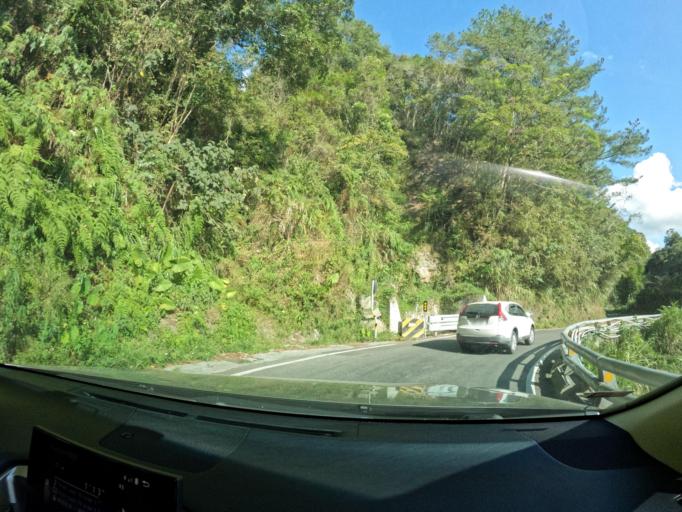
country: TW
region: Taiwan
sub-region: Taitung
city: Taitung
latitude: 23.1923
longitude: 121.0181
